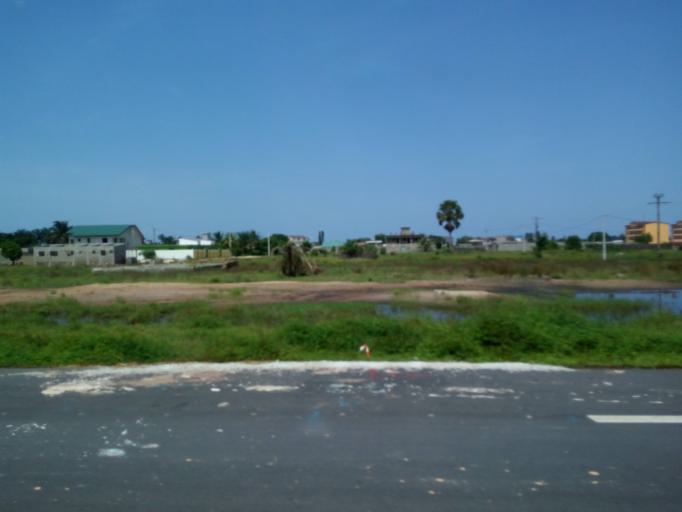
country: CI
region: Sud-Comoe
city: Grand-Bassam
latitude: 5.2249
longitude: -3.7331
